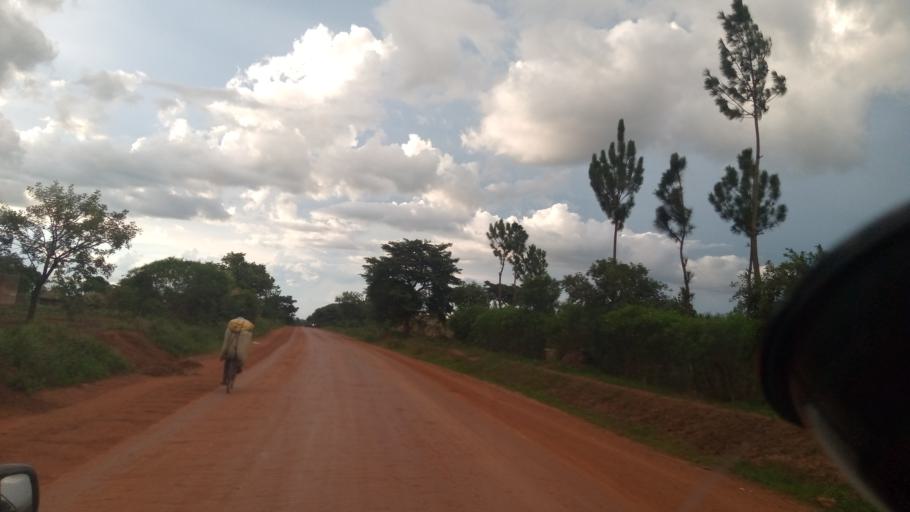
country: UG
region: Northern Region
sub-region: Lira District
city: Lira
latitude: 2.3715
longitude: 32.9354
